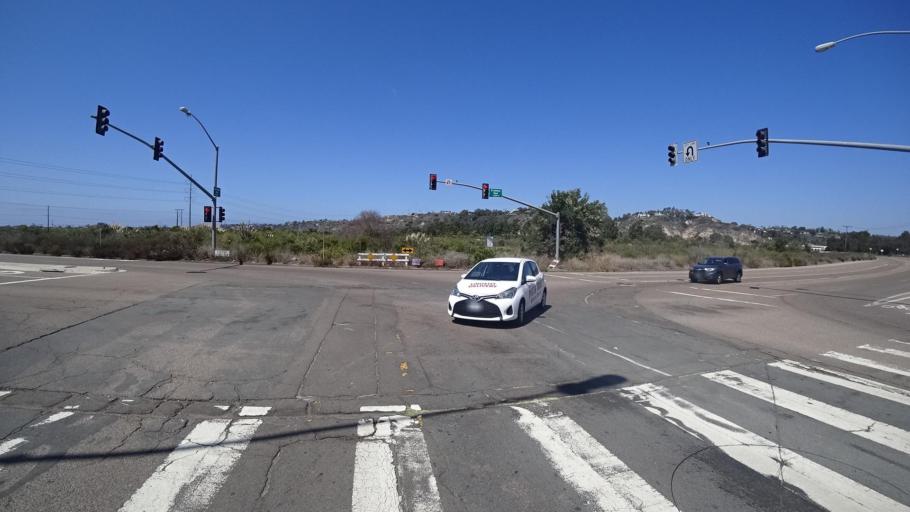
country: US
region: California
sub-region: San Diego County
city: Del Mar
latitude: 32.9757
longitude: -117.2310
